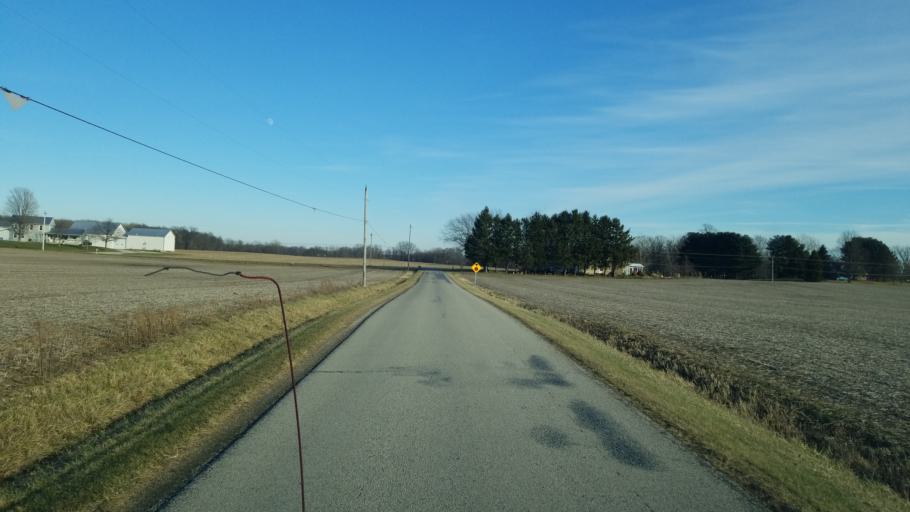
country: US
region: Ohio
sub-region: Huron County
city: Monroeville
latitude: 41.1846
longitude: -82.7043
